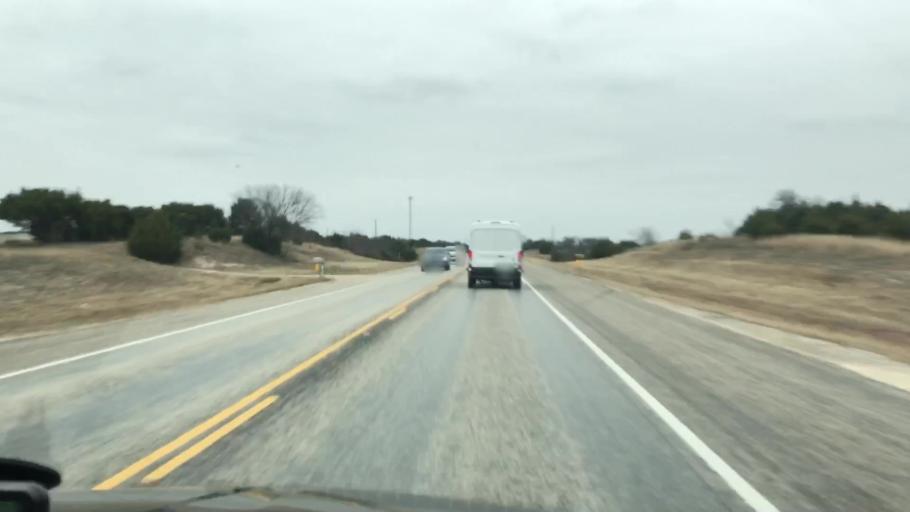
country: US
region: Texas
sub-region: Lampasas County
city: Lampasas
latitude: 31.1255
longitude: -98.1901
